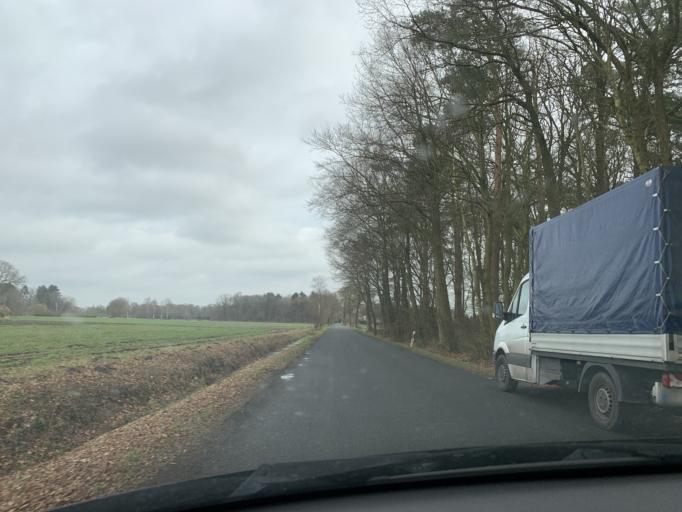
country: DE
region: Lower Saxony
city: Wiefelstede
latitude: 53.1977
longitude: 8.1128
